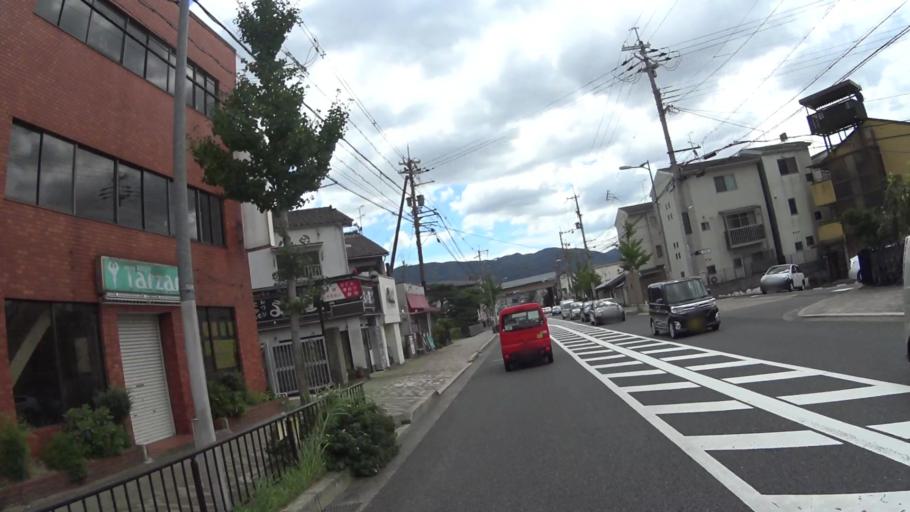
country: JP
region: Kyoto
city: Kyoto
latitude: 34.9939
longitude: 135.8055
